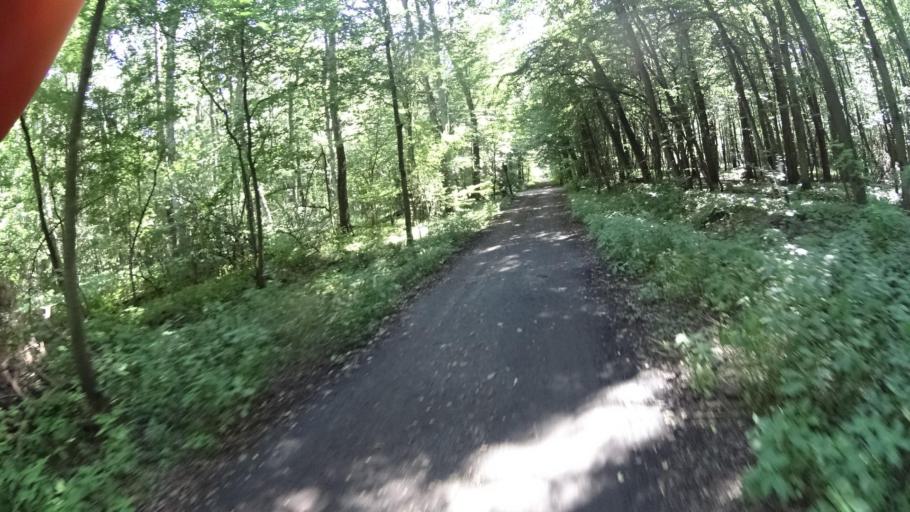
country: PL
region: Masovian Voivodeship
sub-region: Powiat piaseczynski
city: Jozefoslaw
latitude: 52.1159
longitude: 21.0552
